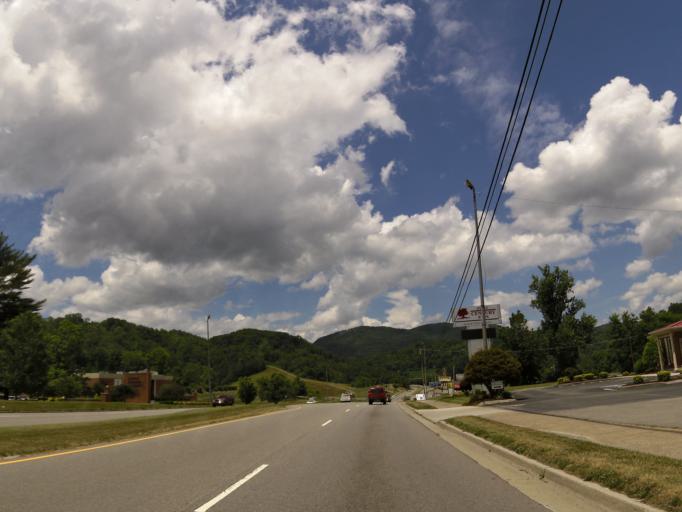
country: US
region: Tennessee
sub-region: Claiborne County
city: Harrogate
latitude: 36.5796
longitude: -83.6561
